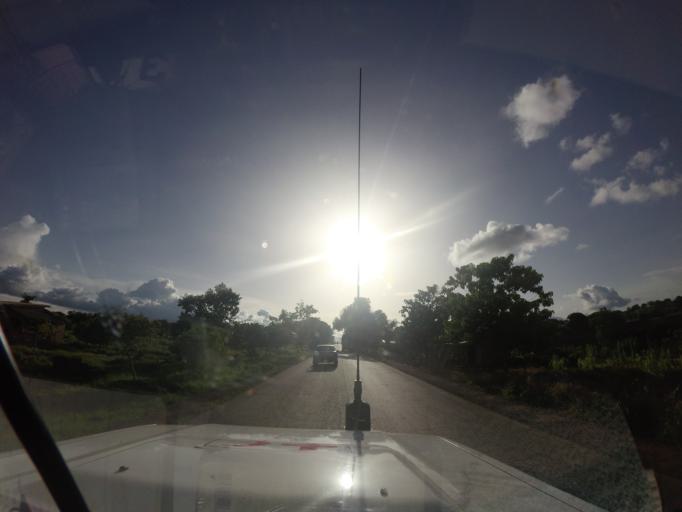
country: GN
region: Kindia
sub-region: Kindia
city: Kindia
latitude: 10.0206
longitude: -12.8342
